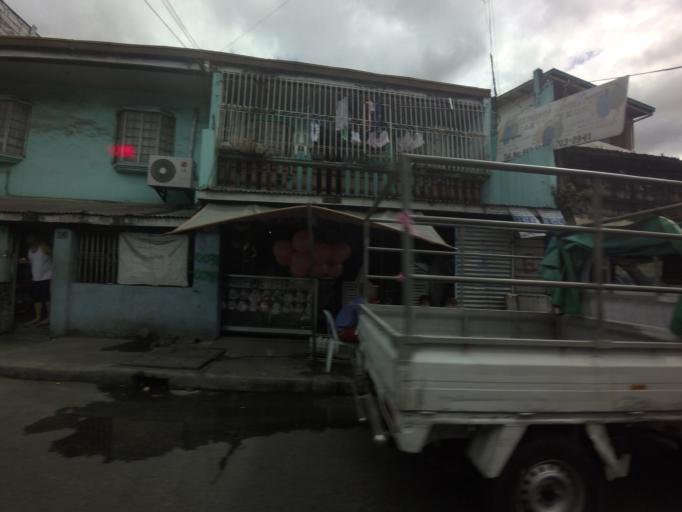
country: PH
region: Calabarzon
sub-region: Province of Rizal
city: Pateros
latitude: 14.5615
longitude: 121.0858
